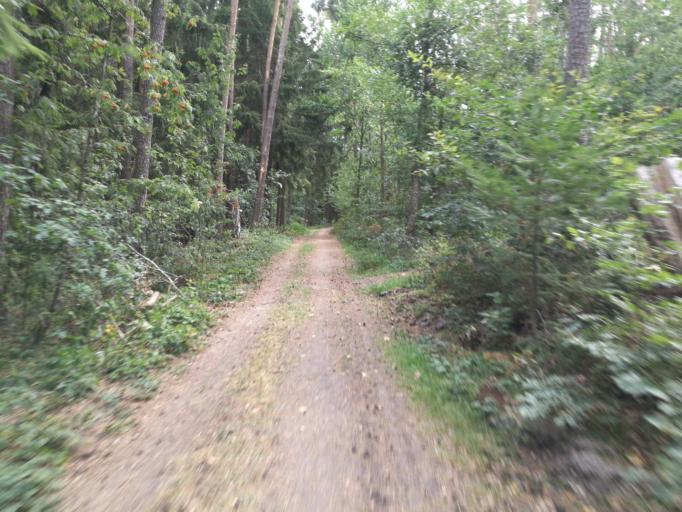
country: DE
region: Bavaria
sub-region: Regierungsbezirk Mittelfranken
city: Seukendorf
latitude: 49.4758
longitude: 10.9106
